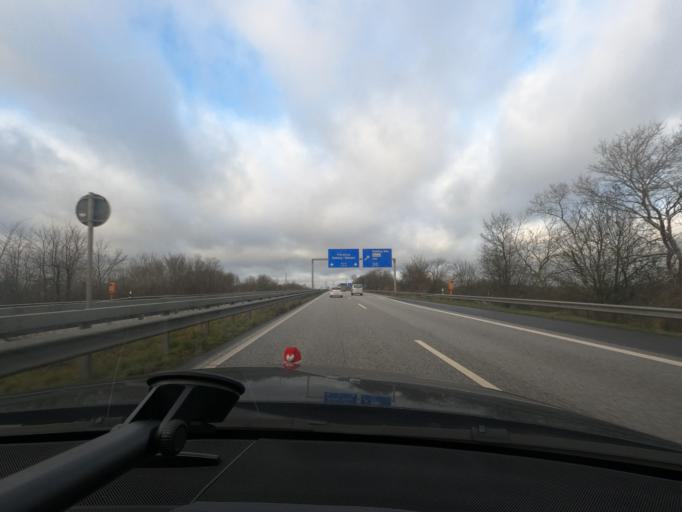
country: DE
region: Schleswig-Holstein
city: Schulldorf
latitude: 54.2987
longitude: 9.7594
